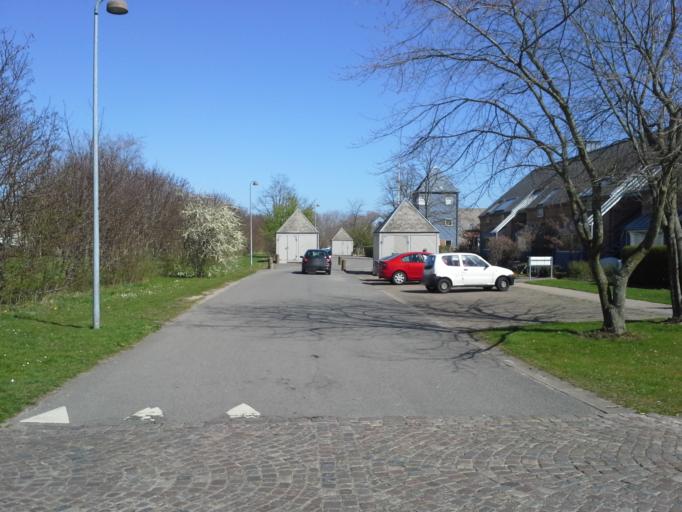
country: DK
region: South Denmark
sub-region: Odense Kommune
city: Neder Holluf
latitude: 55.3791
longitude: 10.4496
